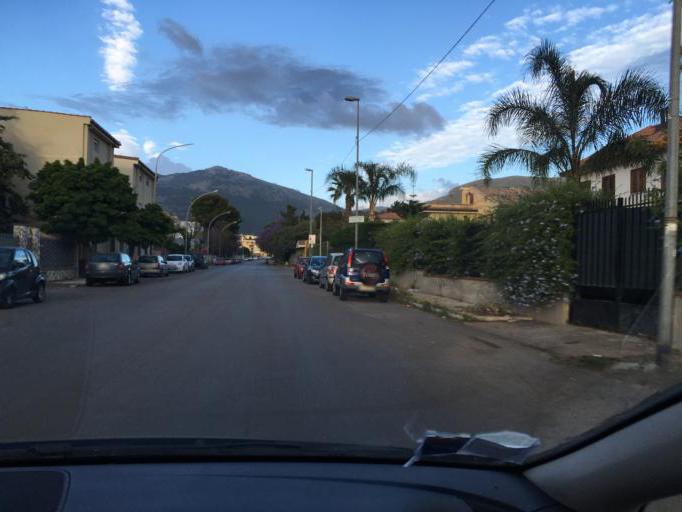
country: IT
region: Sicily
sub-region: Palermo
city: Palermo
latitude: 38.1989
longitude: 13.3166
